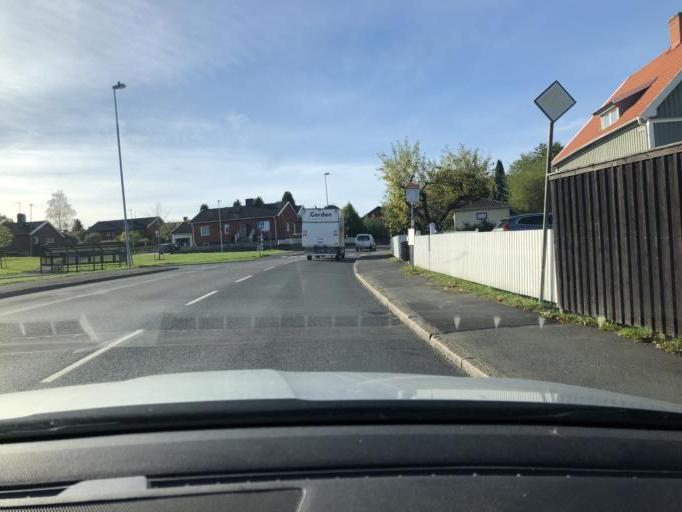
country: SE
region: Joenkoeping
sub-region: Jonkopings Kommun
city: Jonkoping
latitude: 57.7738
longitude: 14.1256
